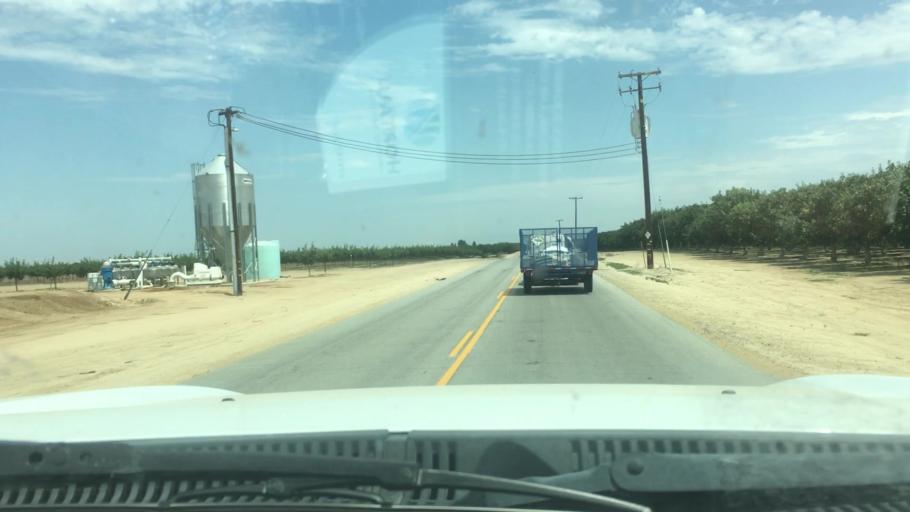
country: US
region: California
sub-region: Kern County
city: McFarland
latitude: 35.5905
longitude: -119.1510
